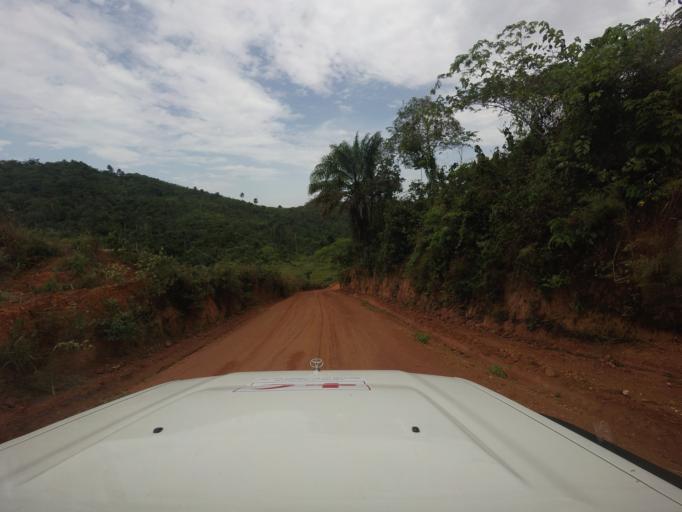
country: SL
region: Eastern Province
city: Buedu
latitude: 8.2229
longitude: -10.2228
